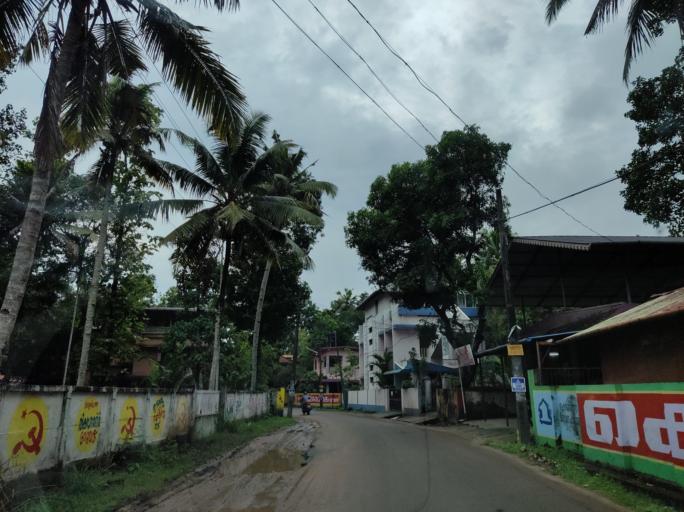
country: IN
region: Kerala
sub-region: Alappuzha
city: Mavelikara
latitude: 9.2419
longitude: 76.5223
